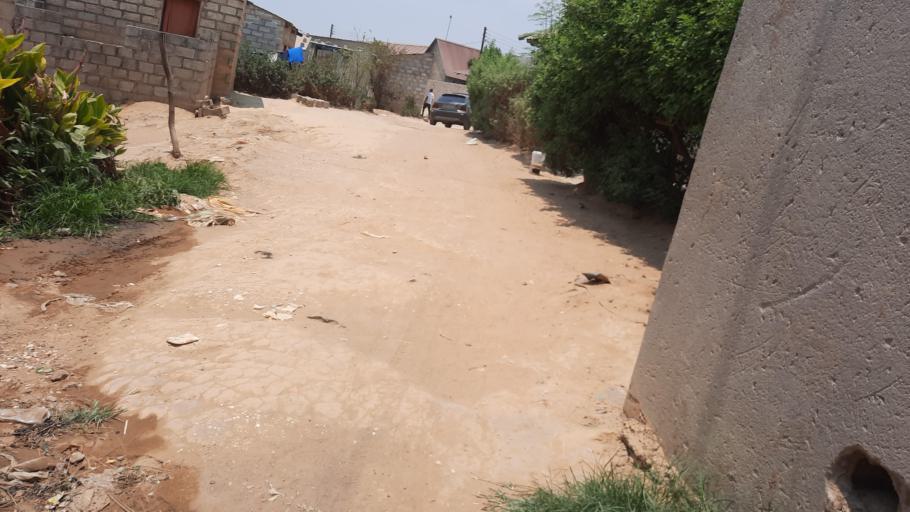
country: ZM
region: Lusaka
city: Lusaka
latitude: -15.4035
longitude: 28.3820
